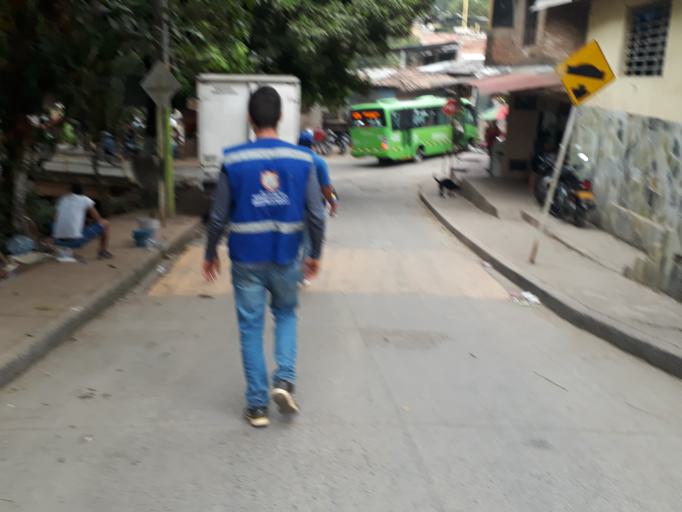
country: CO
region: Valle del Cauca
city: Cali
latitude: 3.4075
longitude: -76.5754
